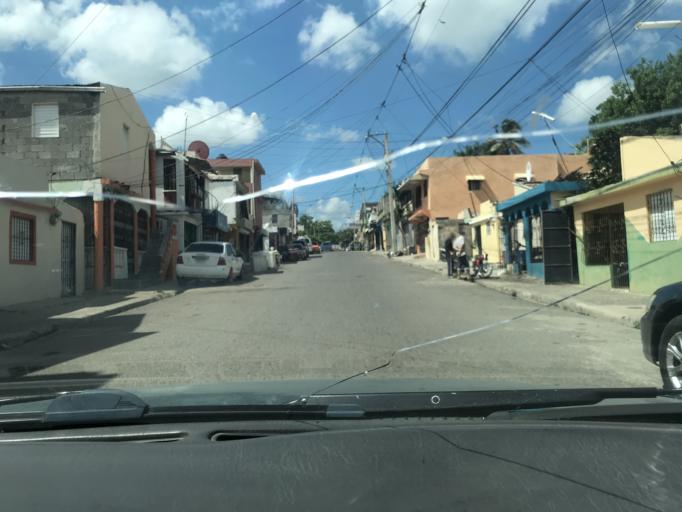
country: DO
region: Santiago
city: Palmar Arriba
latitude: 19.4842
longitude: -70.7468
